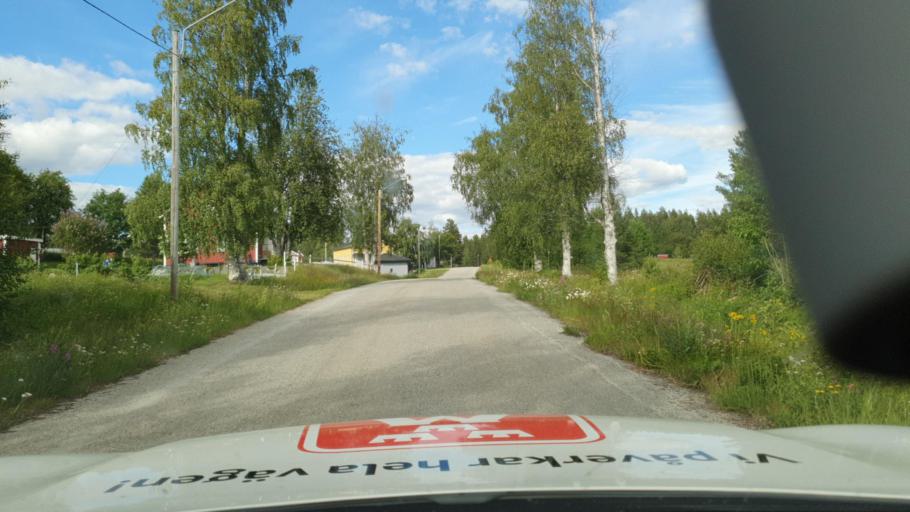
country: SE
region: Vaesterbotten
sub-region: Lycksele Kommun
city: Lycksele
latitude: 64.3738
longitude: 18.5795
